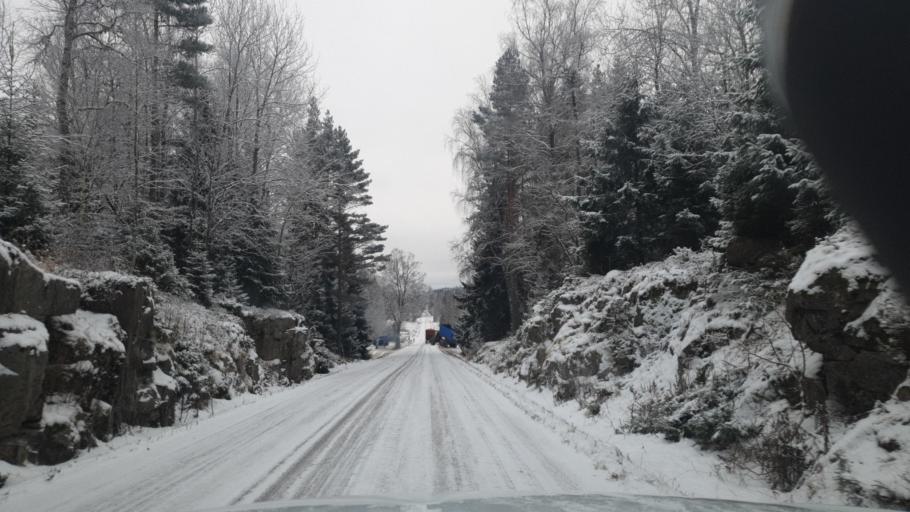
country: NO
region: Ostfold
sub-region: Romskog
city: Romskog
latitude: 59.7393
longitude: 12.0580
